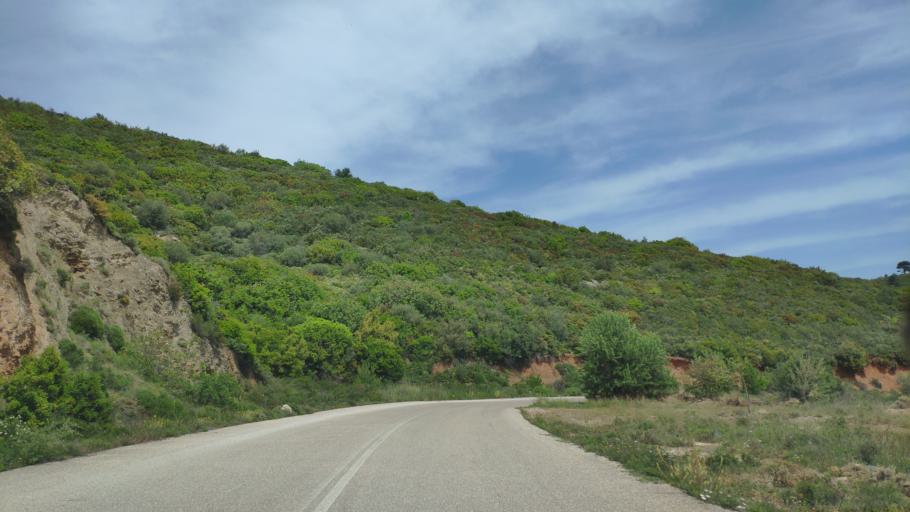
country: GR
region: Attica
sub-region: Nomarchia Anatolikis Attikis
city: Varnavas
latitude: 38.2444
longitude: 23.9580
